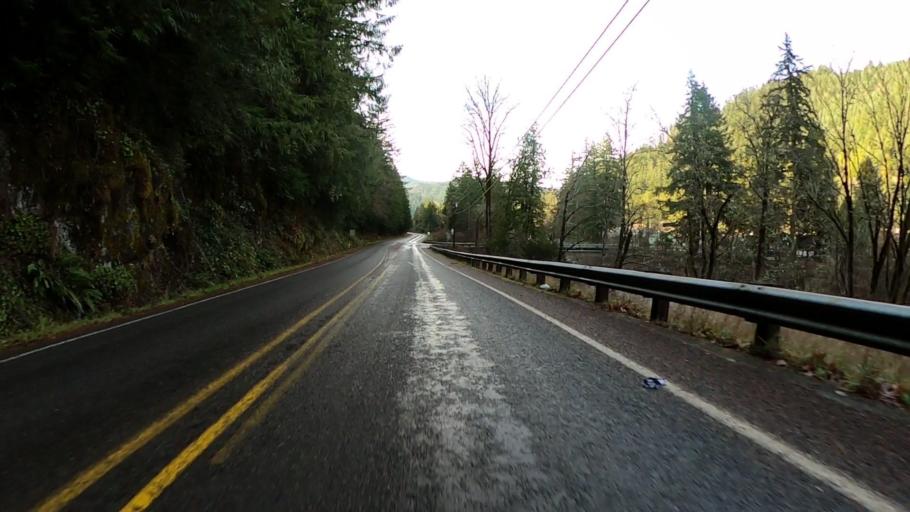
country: US
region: Oregon
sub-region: Lane County
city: Oakridge
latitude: 43.7569
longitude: -122.5110
